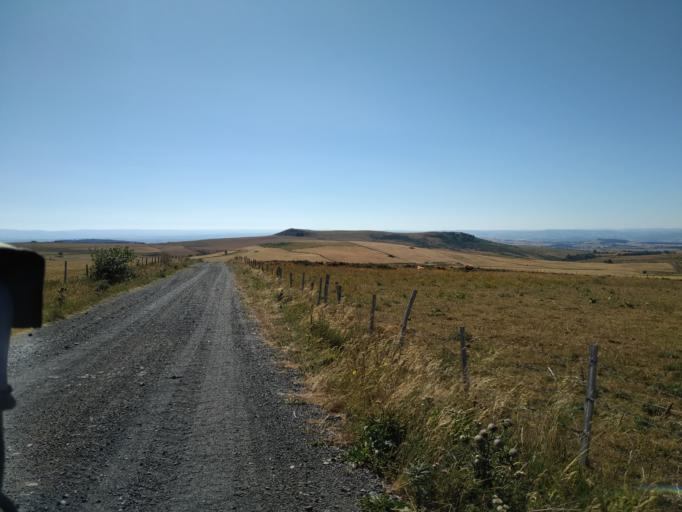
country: FR
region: Auvergne
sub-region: Departement du Cantal
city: Murat
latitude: 45.0214
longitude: 2.8115
